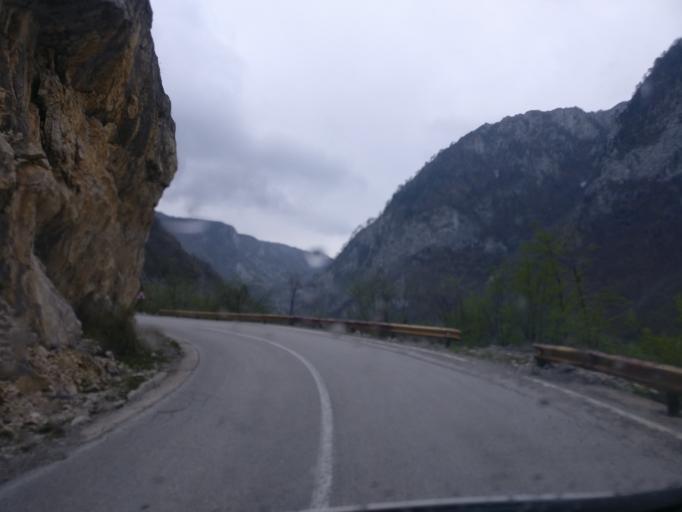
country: ME
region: Opstina Pluzine
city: Pluzine
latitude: 43.2249
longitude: 18.8459
